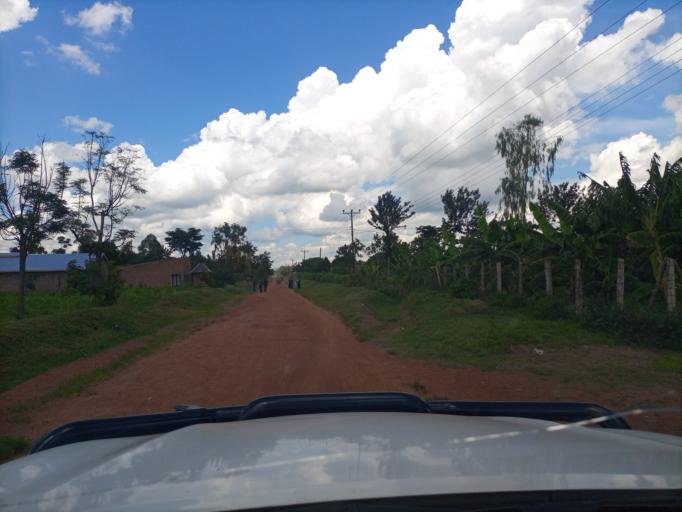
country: UG
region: Eastern Region
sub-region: Tororo District
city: Tororo
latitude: 0.6733
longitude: 34.0048
